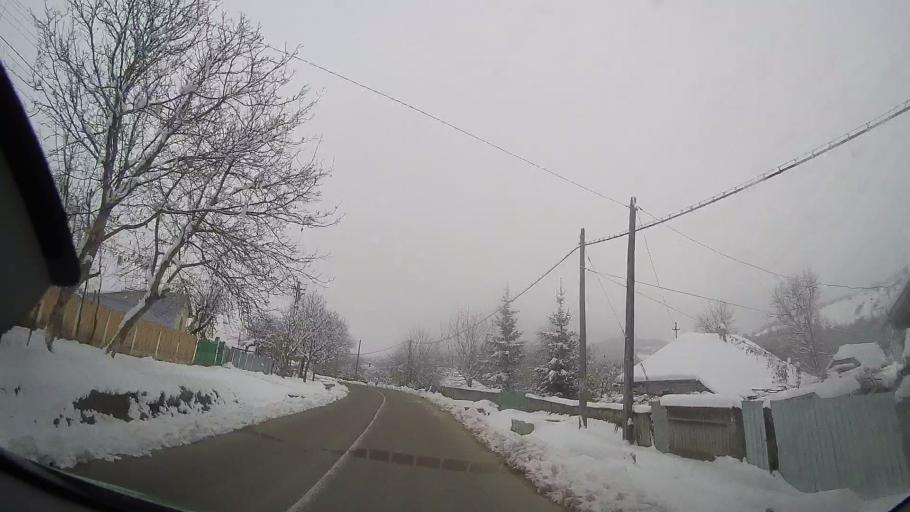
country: RO
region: Neamt
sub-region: Comuna Bozieni
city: Bozieni
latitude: 46.8384
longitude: 27.1508
